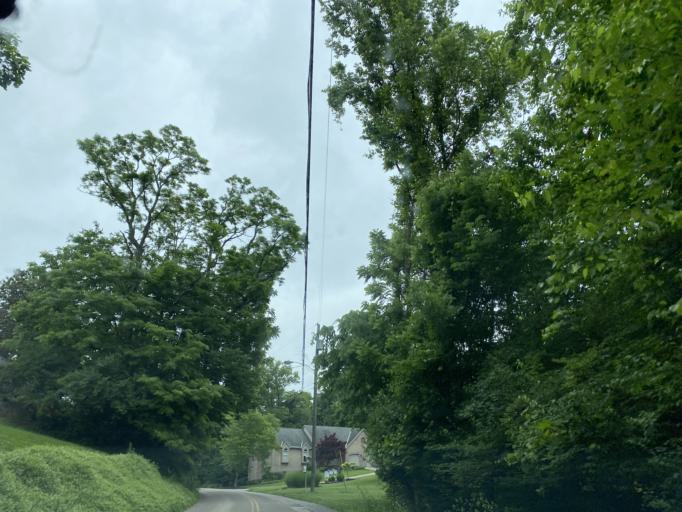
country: US
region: Kentucky
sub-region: Campbell County
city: Dayton
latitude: 39.1009
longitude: -84.4558
